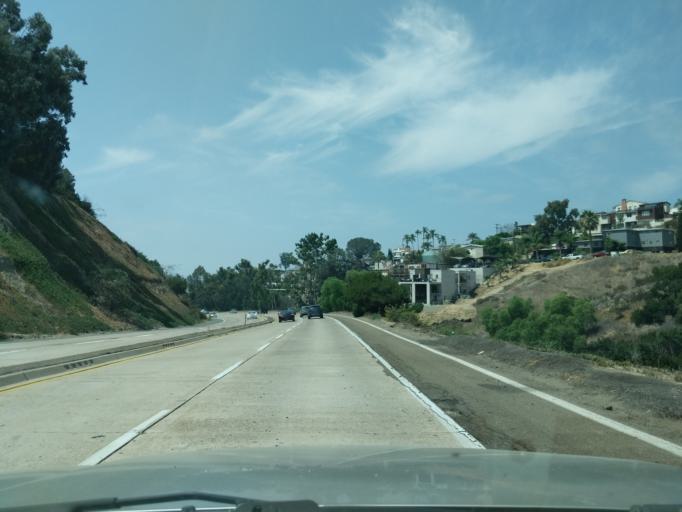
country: US
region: California
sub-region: San Diego County
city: San Diego
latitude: 32.7470
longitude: -117.1774
